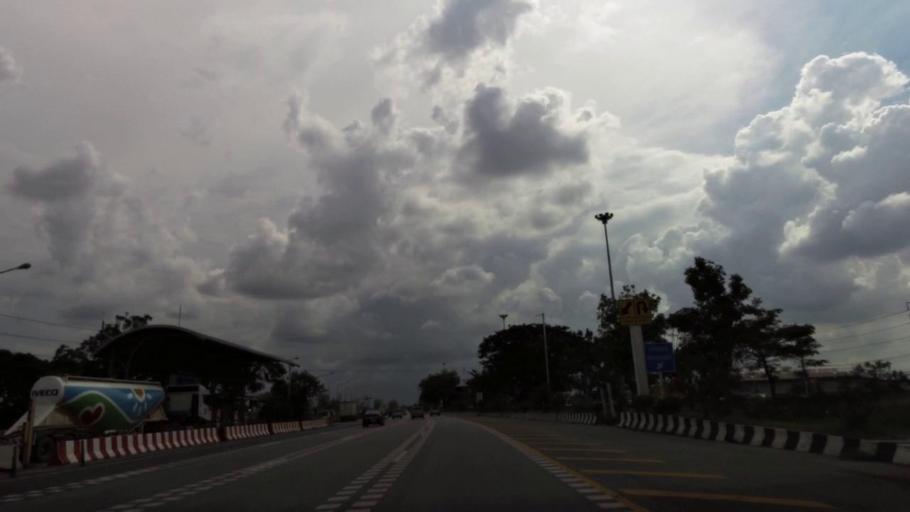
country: TH
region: Phra Nakhon Si Ayutthaya
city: Bang Pa-in
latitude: 14.2076
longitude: 100.6089
